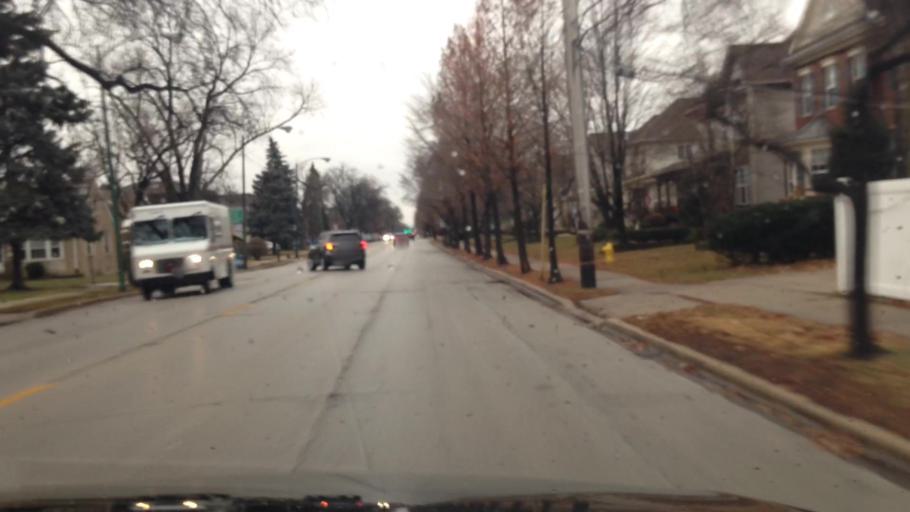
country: US
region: Illinois
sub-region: Cook County
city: Park Ridge
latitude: 41.9907
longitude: -87.8226
